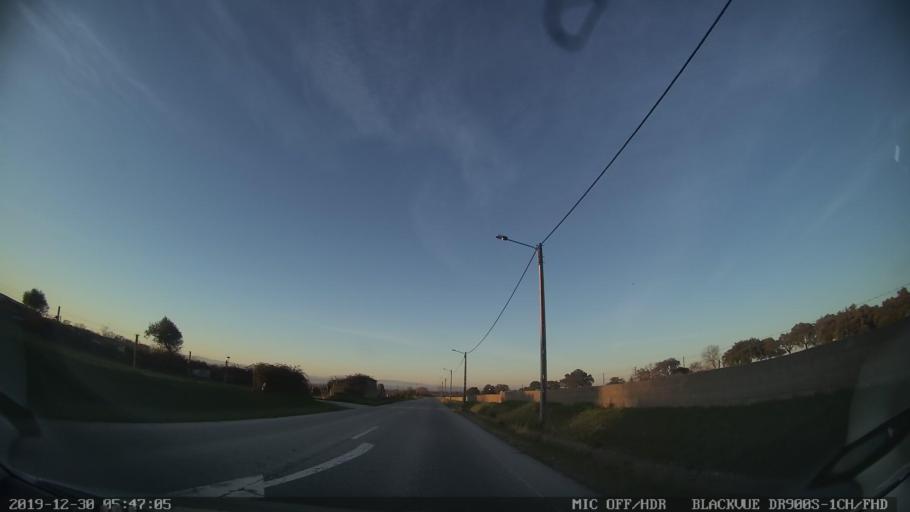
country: PT
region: Castelo Branco
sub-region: Idanha-A-Nova
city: Idanha-a-Nova
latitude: 39.9475
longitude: -7.2378
